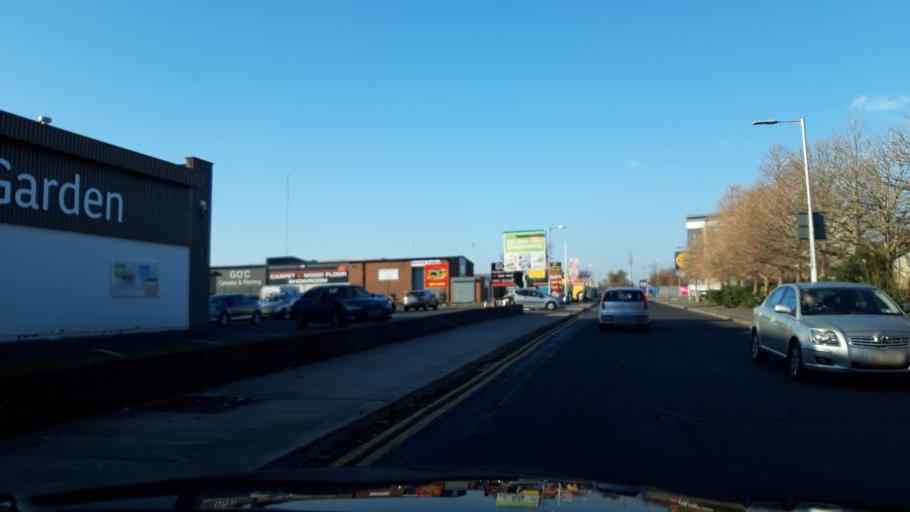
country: IE
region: Leinster
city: Cabra
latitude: 53.3726
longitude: -6.2843
